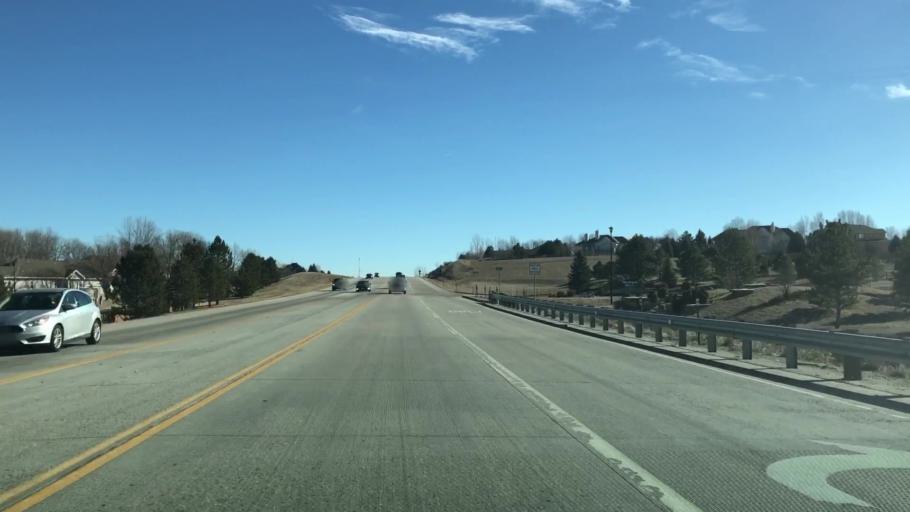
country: US
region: Colorado
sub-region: Weld County
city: Windsor
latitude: 40.4793
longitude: -104.9711
